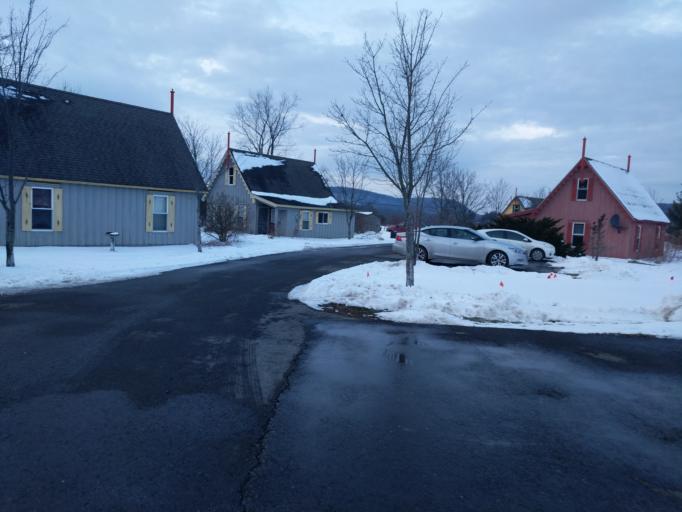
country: US
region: New York
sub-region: Tompkins County
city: Dryden
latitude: 42.3873
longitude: -76.3618
